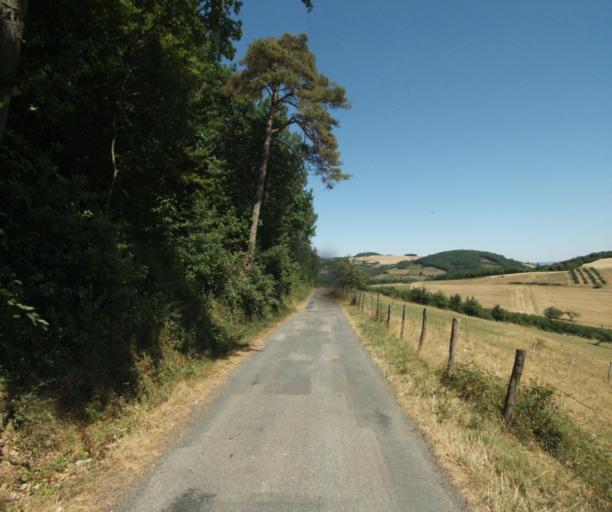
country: FR
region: Rhone-Alpes
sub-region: Departement du Rhone
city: Bessenay
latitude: 45.7814
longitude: 4.5243
